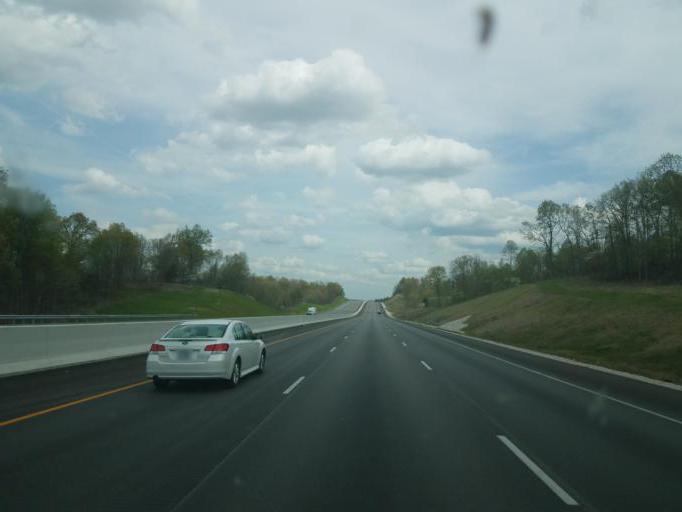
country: US
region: Kentucky
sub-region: Hart County
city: Munfordville
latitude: 37.3479
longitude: -85.9023
